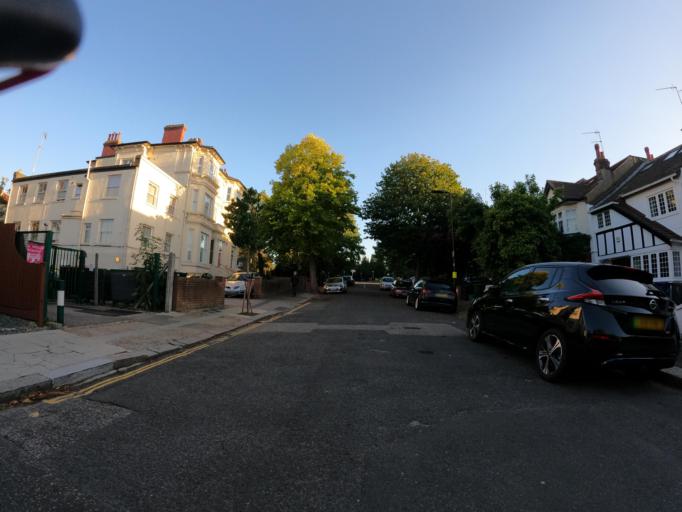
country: GB
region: England
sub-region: Greater London
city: Ealing Broadway
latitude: 51.5257
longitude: -0.3187
